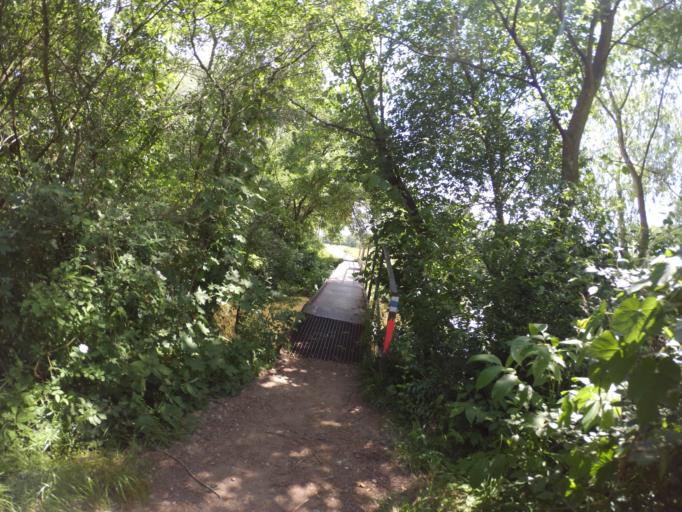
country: CZ
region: Central Bohemia
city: Milovice
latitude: 50.1711
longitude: 14.9038
